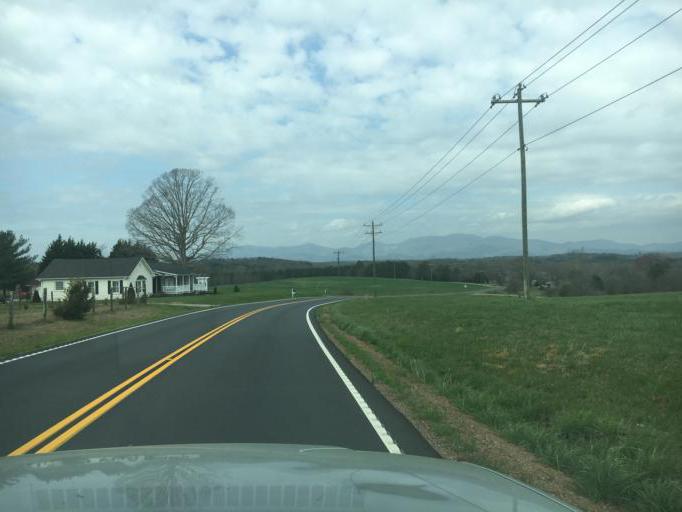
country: US
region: South Carolina
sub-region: Spartanburg County
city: Inman Mills
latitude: 35.0798
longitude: -82.1867
